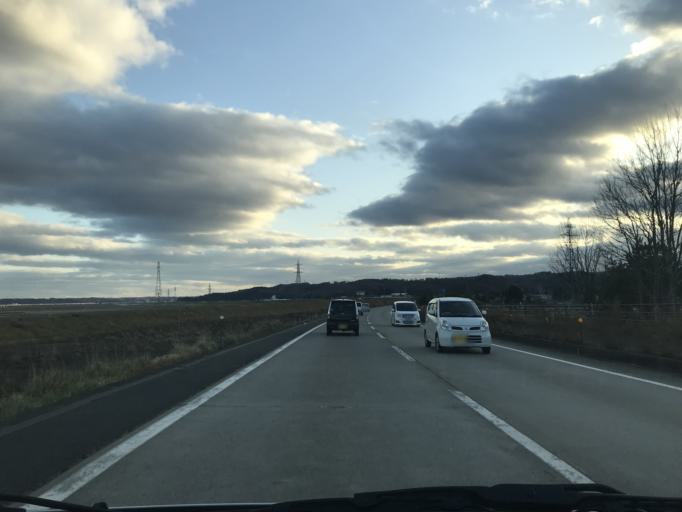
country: JP
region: Iwate
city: Ichinoseki
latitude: 38.9844
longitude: 141.1237
